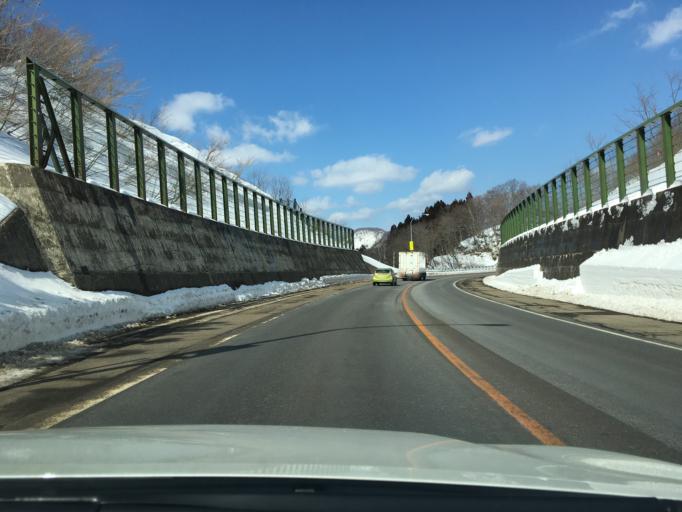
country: JP
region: Yamagata
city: Tsuruoka
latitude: 38.5578
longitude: 139.9288
